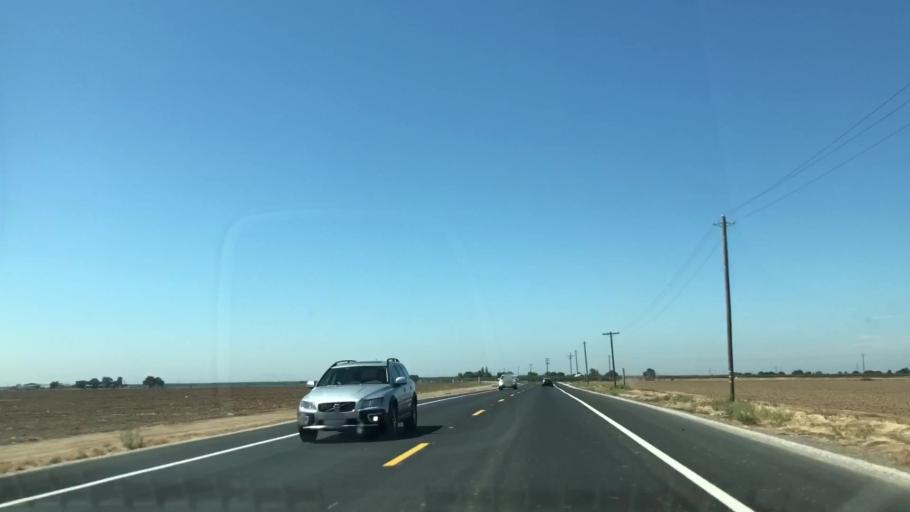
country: US
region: California
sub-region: San Joaquin County
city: Linden
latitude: 37.9410
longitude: -121.1084
